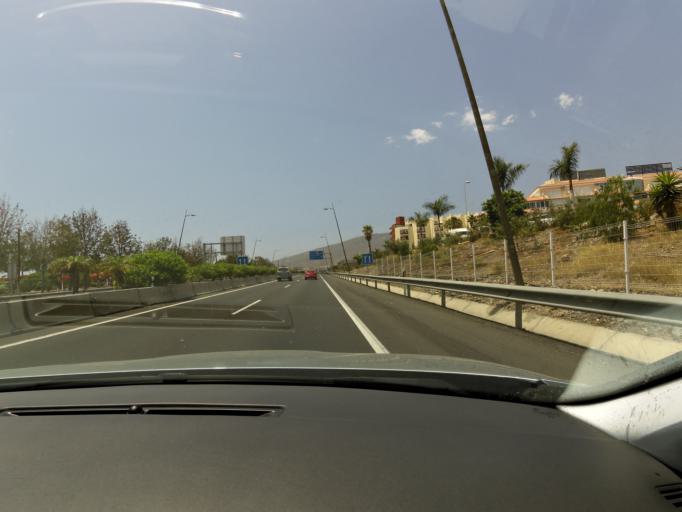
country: ES
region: Canary Islands
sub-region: Provincia de Santa Cruz de Tenerife
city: Adeje
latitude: 28.0936
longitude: -16.7297
